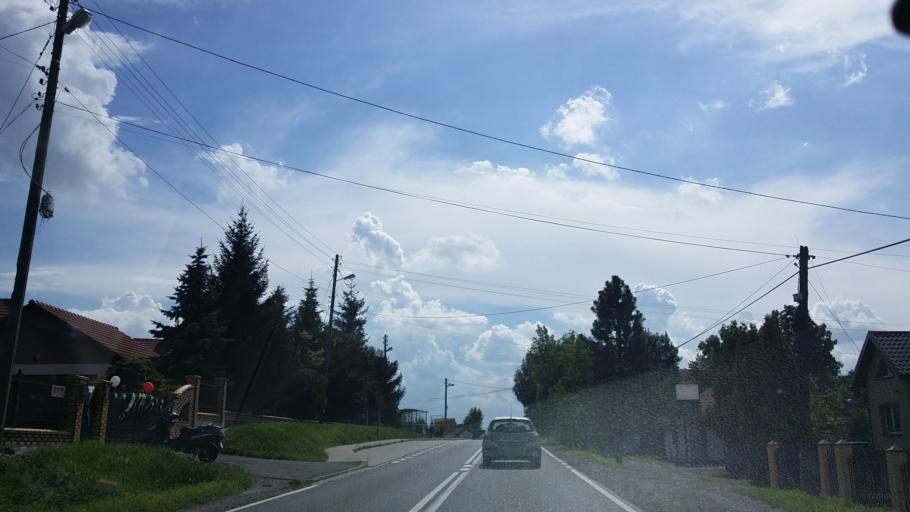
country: PL
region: Lesser Poland Voivodeship
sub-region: Powiat wielicki
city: Pawlikowice
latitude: 49.9600
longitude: 20.0546
